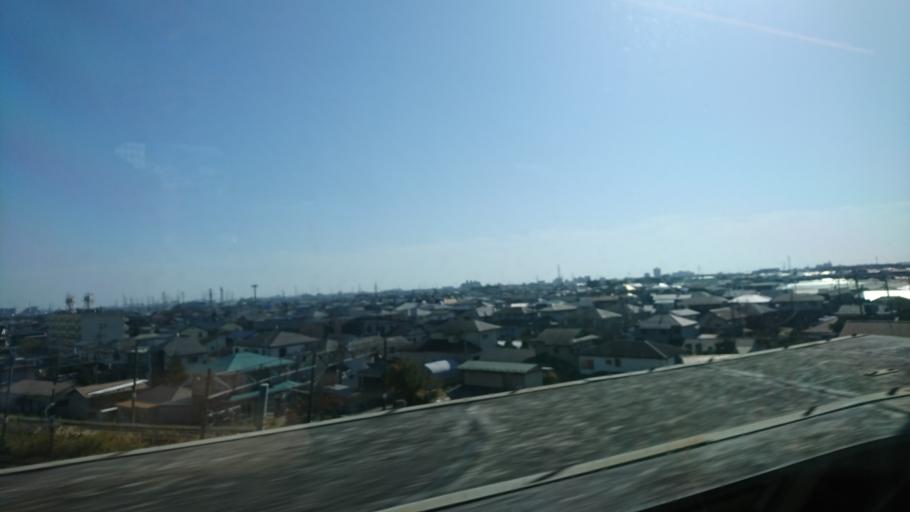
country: JP
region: Miyagi
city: Rifu
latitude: 38.3016
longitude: 140.9571
